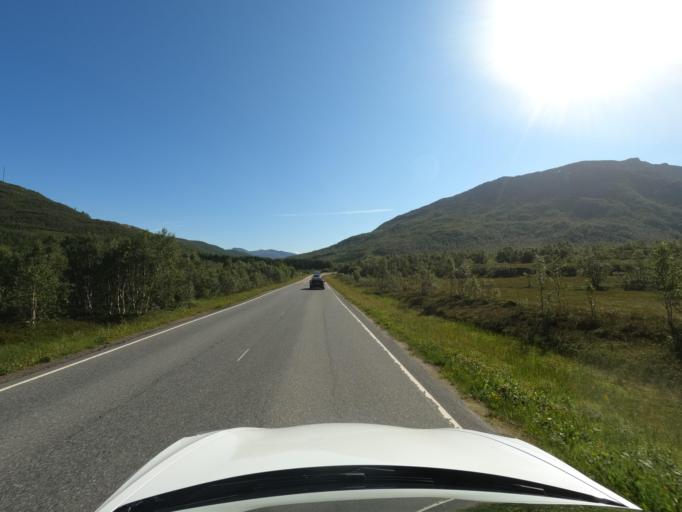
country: NO
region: Nordland
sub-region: Lodingen
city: Lodingen
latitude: 68.5297
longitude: 15.7431
